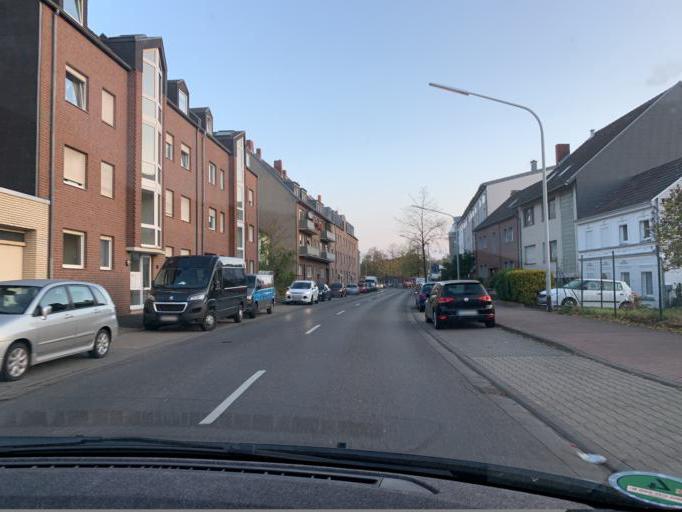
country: DE
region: North Rhine-Westphalia
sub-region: Regierungsbezirk Dusseldorf
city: Monchengladbach
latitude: 51.1373
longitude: 6.4488
